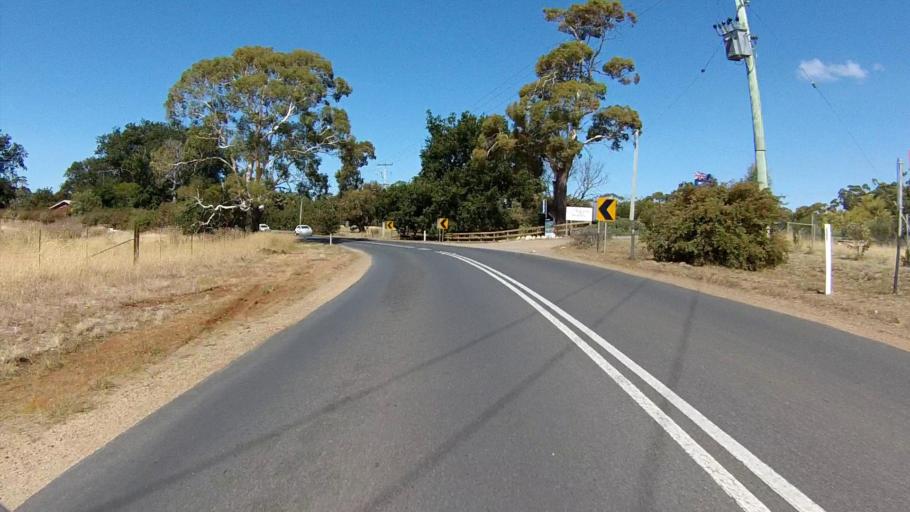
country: AU
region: Tasmania
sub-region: Break O'Day
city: St Helens
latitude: -42.1138
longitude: 148.0561
